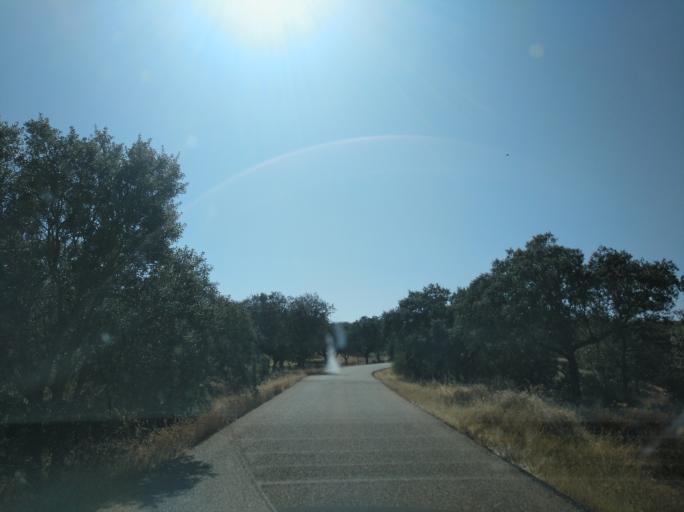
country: PT
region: Portalegre
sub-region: Elvas
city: Elvas
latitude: 38.9893
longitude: -7.1706
